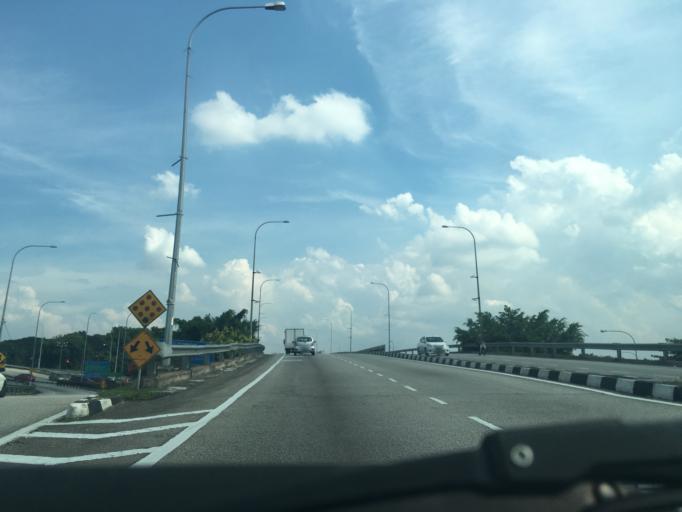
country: MY
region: Perak
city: Ipoh
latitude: 4.6122
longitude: 101.0788
